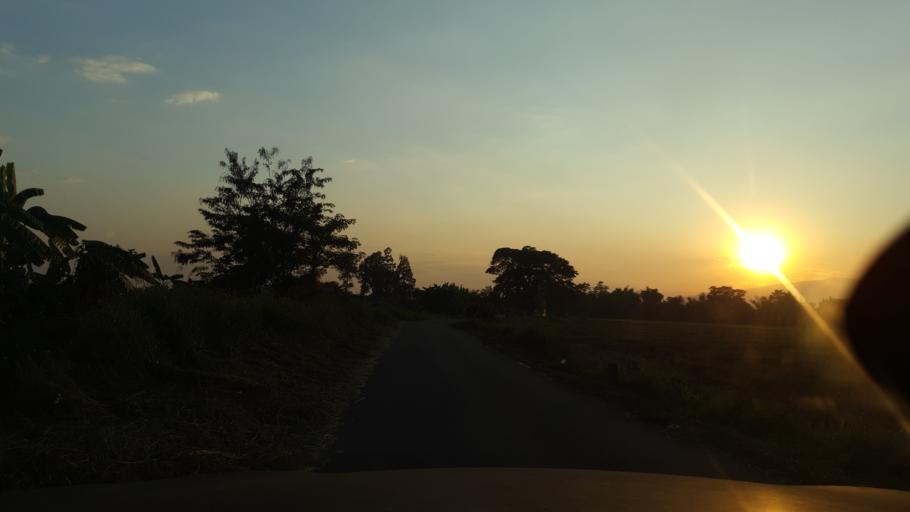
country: TH
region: Chiang Mai
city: San Sai
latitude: 18.8763
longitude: 99.0852
